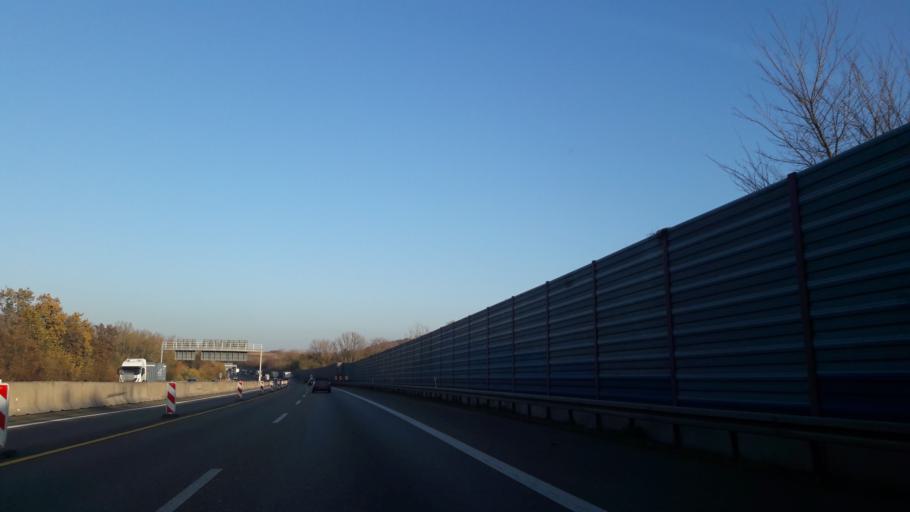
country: DE
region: Baden-Wuerttemberg
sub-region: Karlsruhe Region
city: Rauenberg
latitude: 49.2753
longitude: 8.6965
